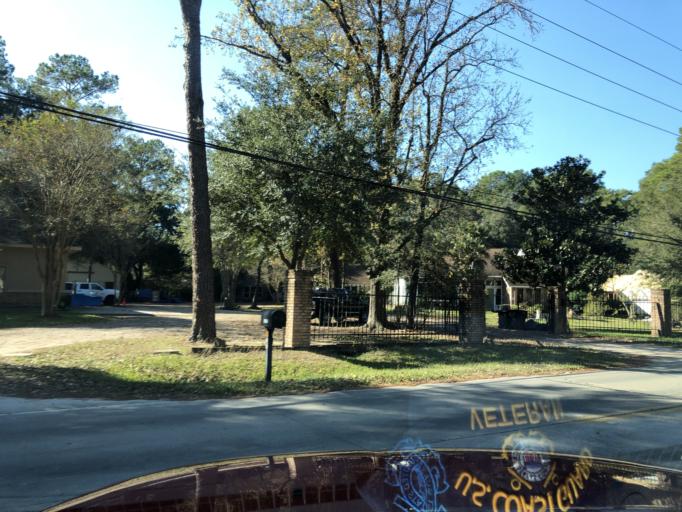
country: US
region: Texas
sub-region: Harris County
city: Tomball
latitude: 30.0283
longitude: -95.5435
